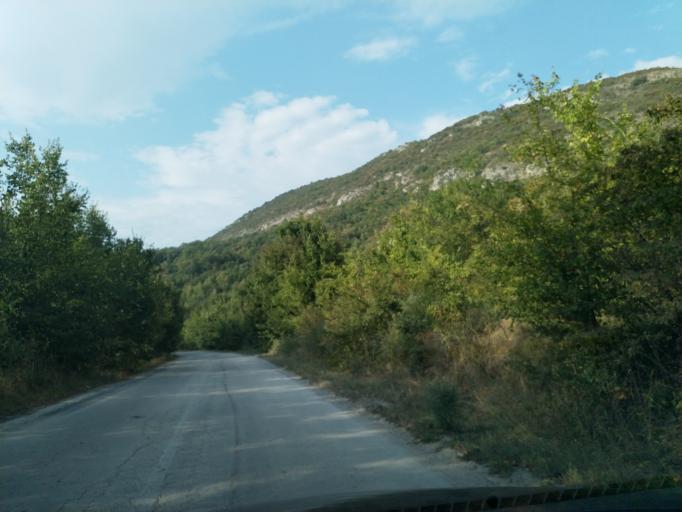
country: RS
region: Central Serbia
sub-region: Pomoravski Okrug
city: Paracin
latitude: 43.8392
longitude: 21.5388
